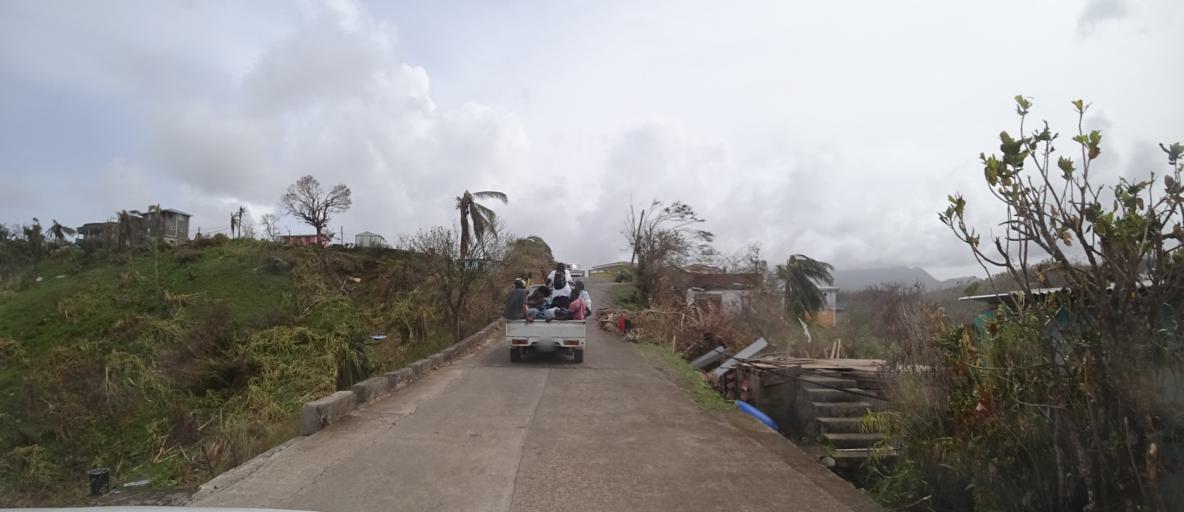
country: DM
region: Saint Andrew
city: Calibishie
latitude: 15.5860
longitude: -61.3746
